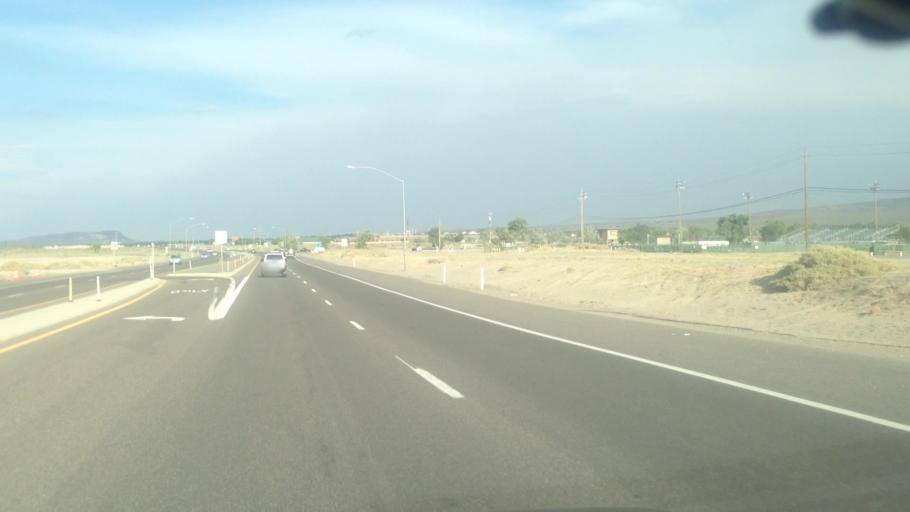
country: US
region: Nevada
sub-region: Lyon County
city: Fernley
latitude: 39.6023
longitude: -119.2243
